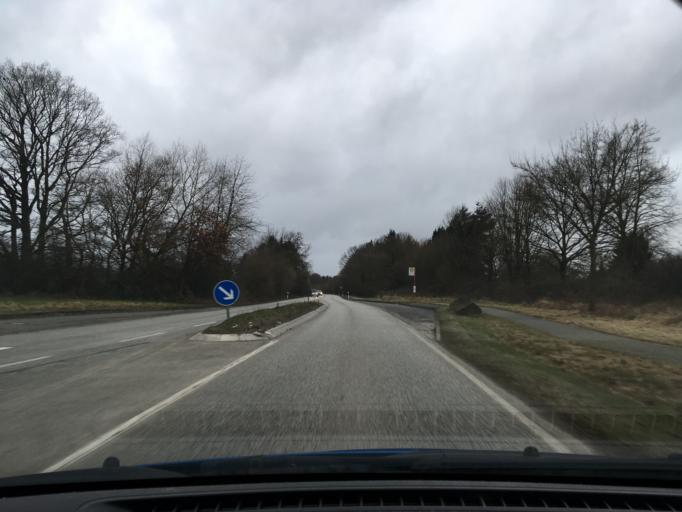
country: DE
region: Schleswig-Holstein
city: Grabau
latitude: 53.4908
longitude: 10.5170
